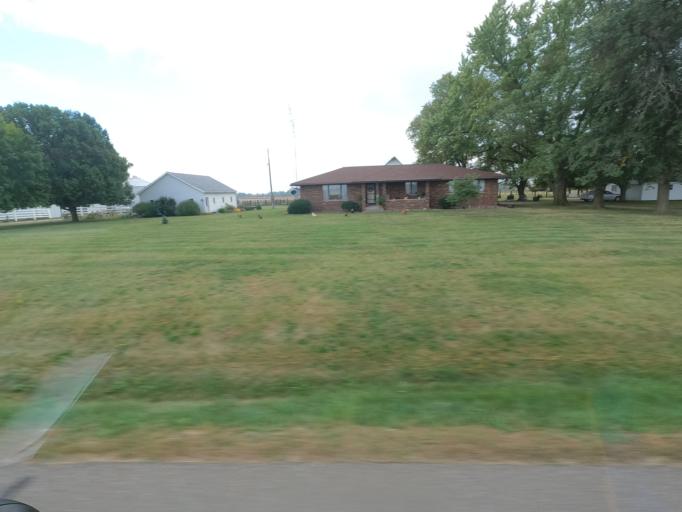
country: US
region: Iowa
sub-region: Henry County
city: Mount Pleasant
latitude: 40.7846
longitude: -91.6151
